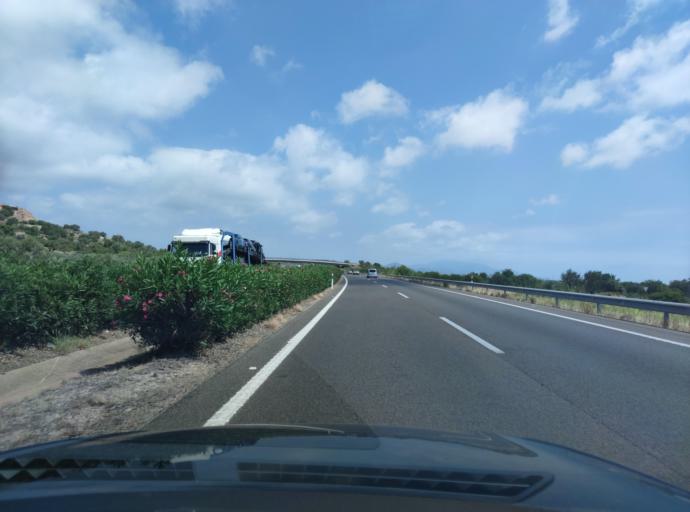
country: ES
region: Valencia
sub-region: Provincia de Castello
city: Benicarlo
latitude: 40.4711
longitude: 0.4178
